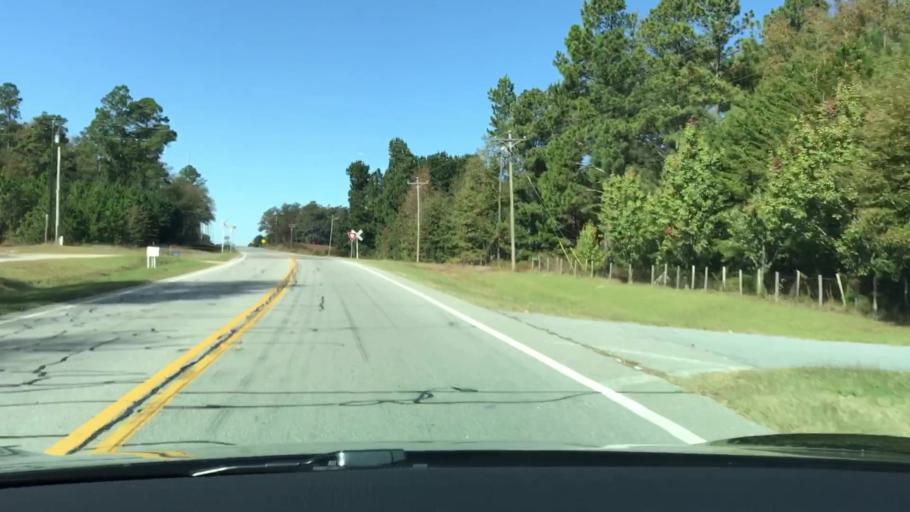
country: US
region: Georgia
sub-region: Warren County
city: Warrenton
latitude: 33.3864
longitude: -82.6324
